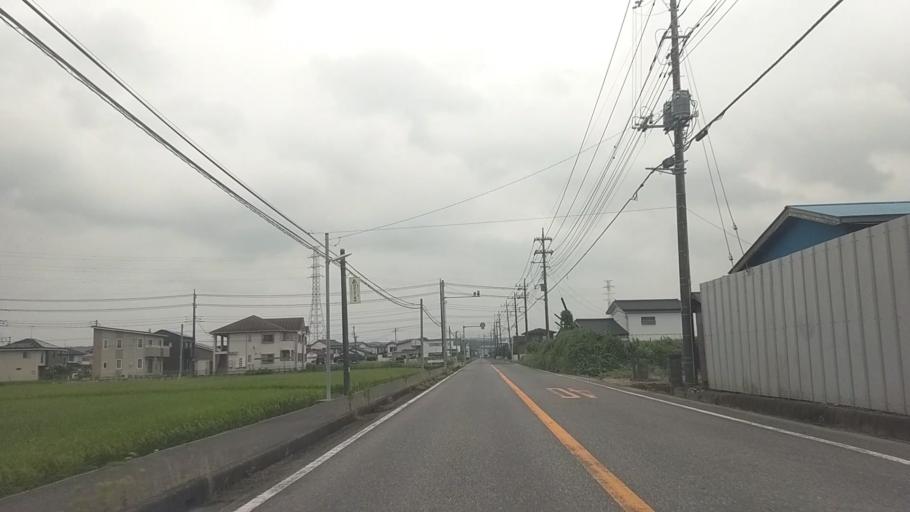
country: JP
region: Chiba
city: Kisarazu
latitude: 35.3866
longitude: 140.0377
